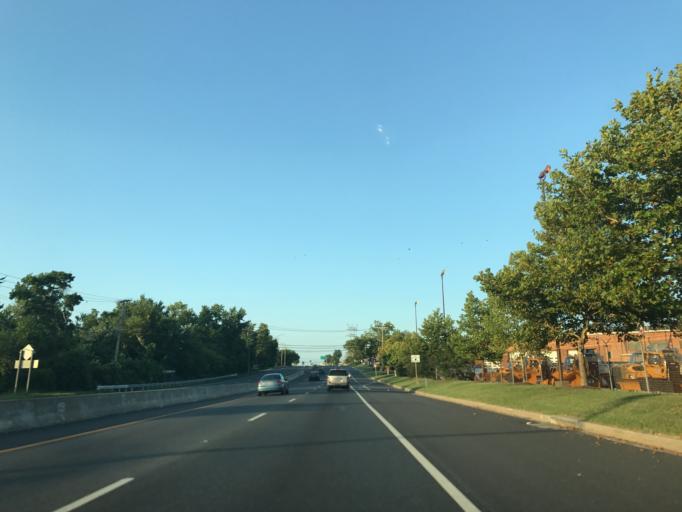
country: US
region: Maryland
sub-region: Baltimore County
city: Rosedale
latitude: 39.3264
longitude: -76.4966
